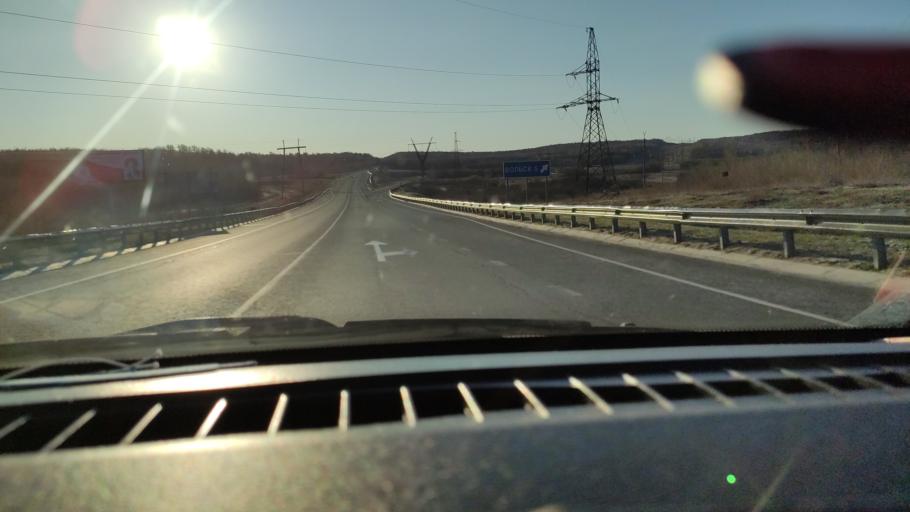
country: RU
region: Saratov
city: Shikhany
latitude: 52.1150
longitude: 47.2988
